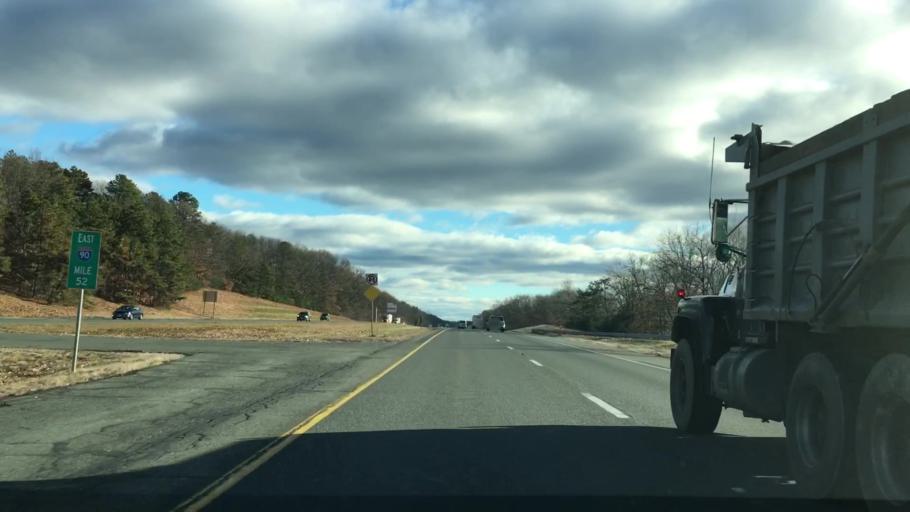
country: US
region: Massachusetts
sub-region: Hampden County
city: Ludlow
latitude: 42.1624
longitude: -72.5259
